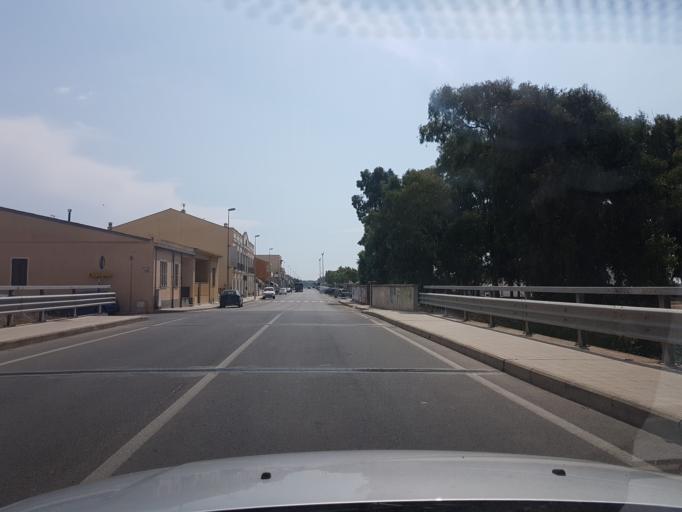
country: IT
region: Sardinia
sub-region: Provincia di Oristano
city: Cabras
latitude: 39.9256
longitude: 8.5270
